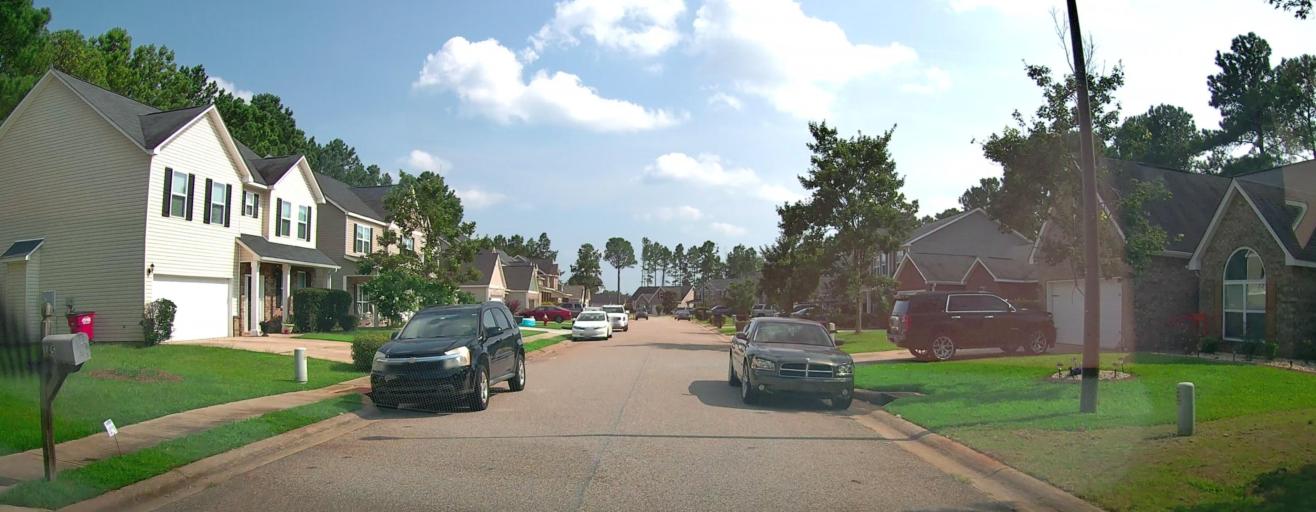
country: US
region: Georgia
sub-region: Houston County
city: Centerville
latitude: 32.6519
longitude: -83.7062
